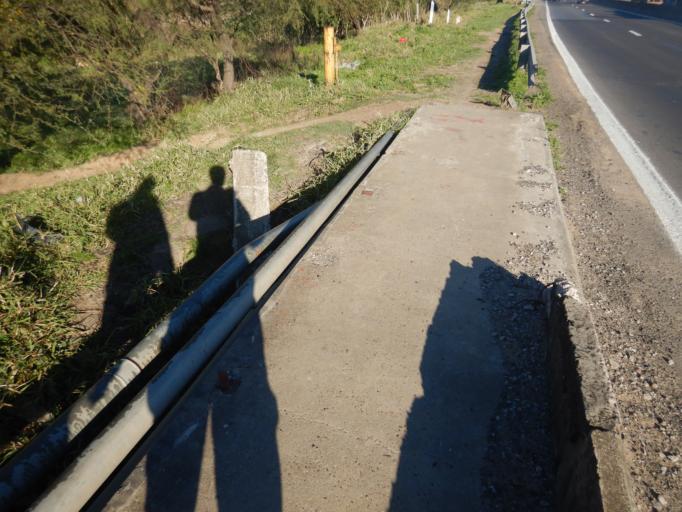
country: AR
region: Santa Fe
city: Santa Fe de la Vera Cruz
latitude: -31.6401
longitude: -60.6433
